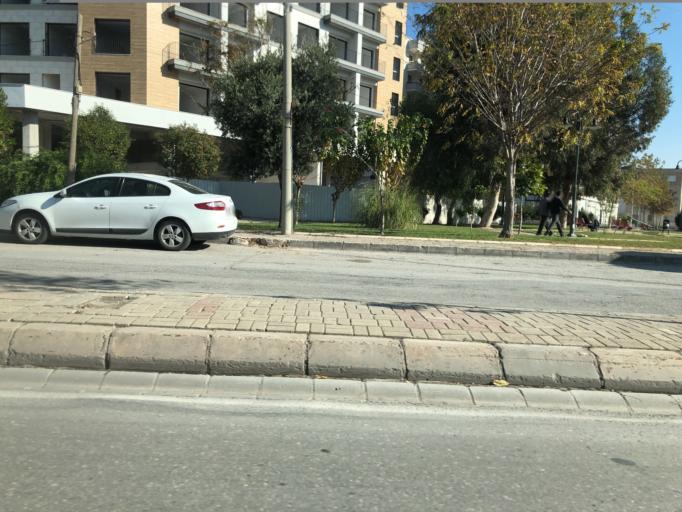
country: TR
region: Izmir
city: Izmir
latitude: 38.4588
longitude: 27.1747
